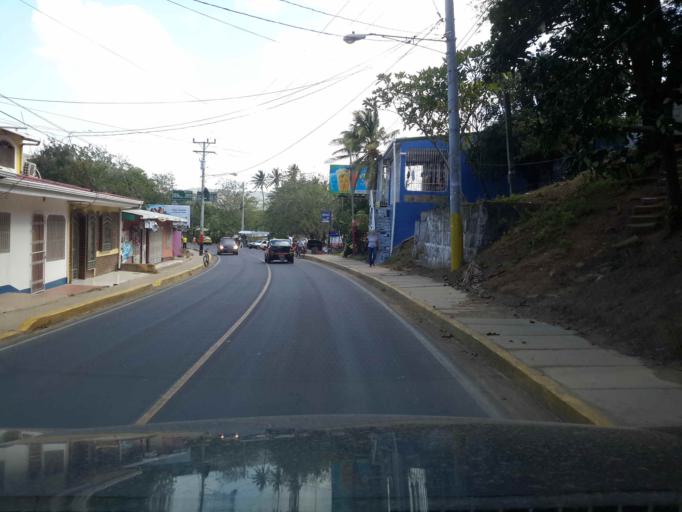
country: NI
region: Rivas
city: San Juan del Sur
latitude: 11.2569
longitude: -85.8657
